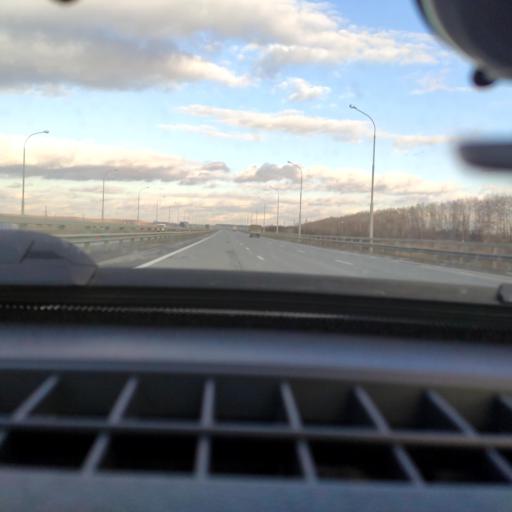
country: RU
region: Bashkortostan
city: Kabakovo
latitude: 54.6573
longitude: 56.1263
